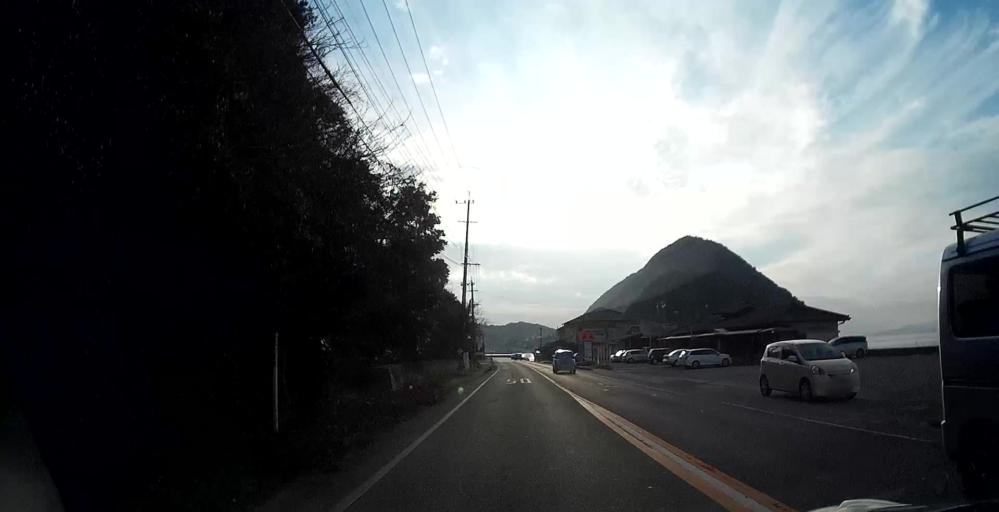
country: JP
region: Nagasaki
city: Shimabara
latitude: 32.6274
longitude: 130.4542
